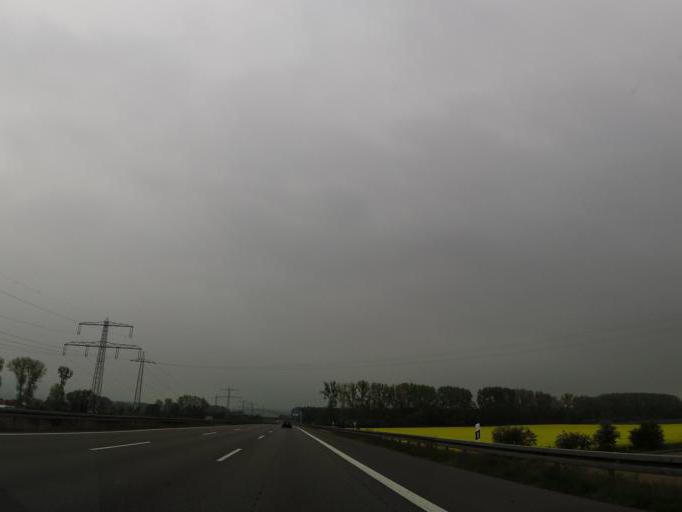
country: DE
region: Lower Saxony
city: Rosdorf
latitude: 51.5097
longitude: 9.8782
